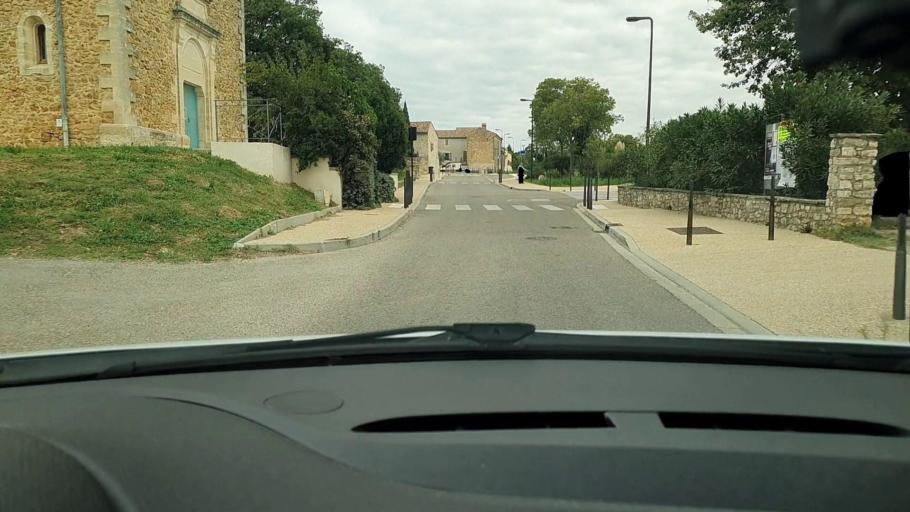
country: FR
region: Languedoc-Roussillon
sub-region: Departement du Gard
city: Saint-Chaptes
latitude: 44.0416
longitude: 4.2982
